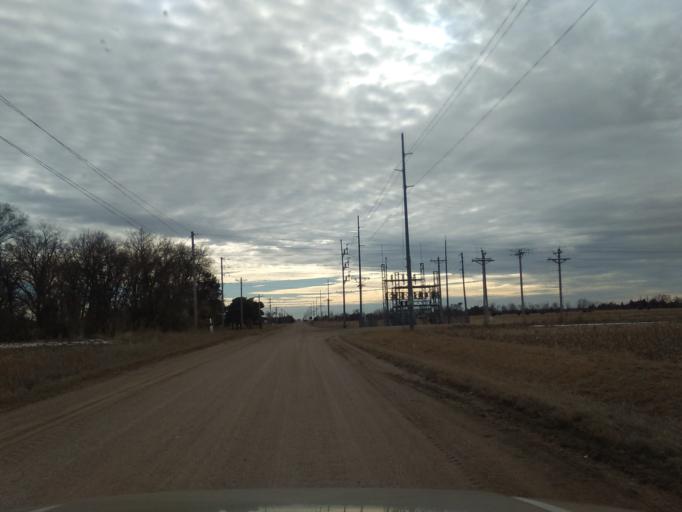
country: US
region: Nebraska
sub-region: Buffalo County
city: Gibbon
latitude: 40.6414
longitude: -98.8759
